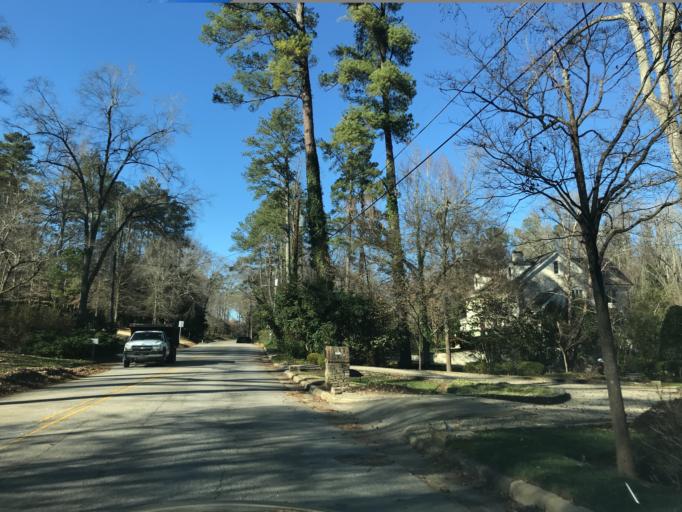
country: US
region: North Carolina
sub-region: Wake County
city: West Raleigh
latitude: 35.8200
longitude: -78.6458
